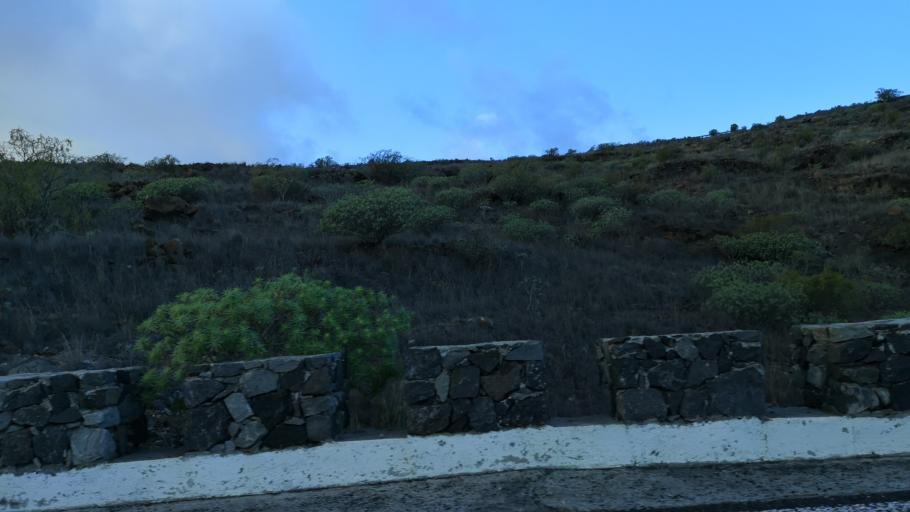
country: ES
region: Canary Islands
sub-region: Provincia de Santa Cruz de Tenerife
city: Alajero
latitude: 28.0406
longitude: -17.2309
